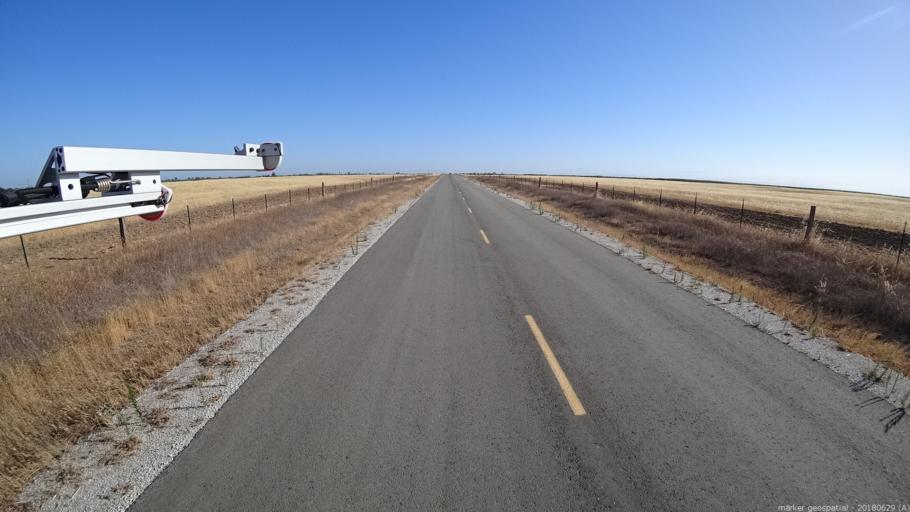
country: US
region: California
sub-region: Madera County
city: Parksdale
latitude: 36.9615
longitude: -120.0016
